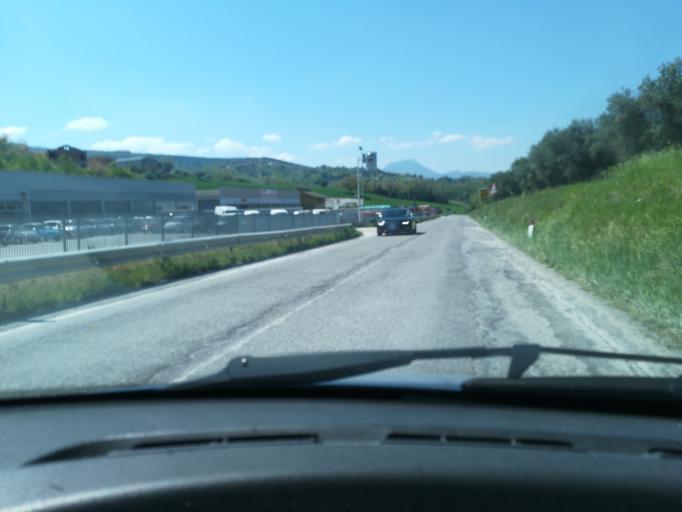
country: IT
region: The Marches
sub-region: Provincia di Macerata
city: Strada
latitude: 43.4010
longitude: 13.2080
